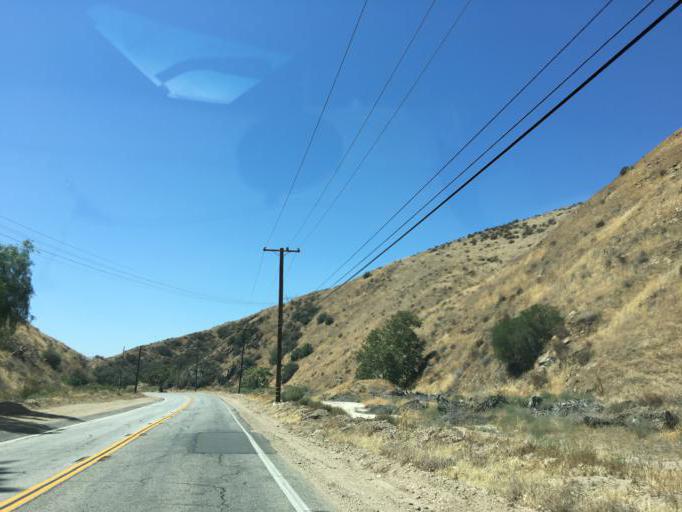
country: US
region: California
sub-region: Los Angeles County
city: Agua Dulce
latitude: 34.4926
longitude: -118.3865
